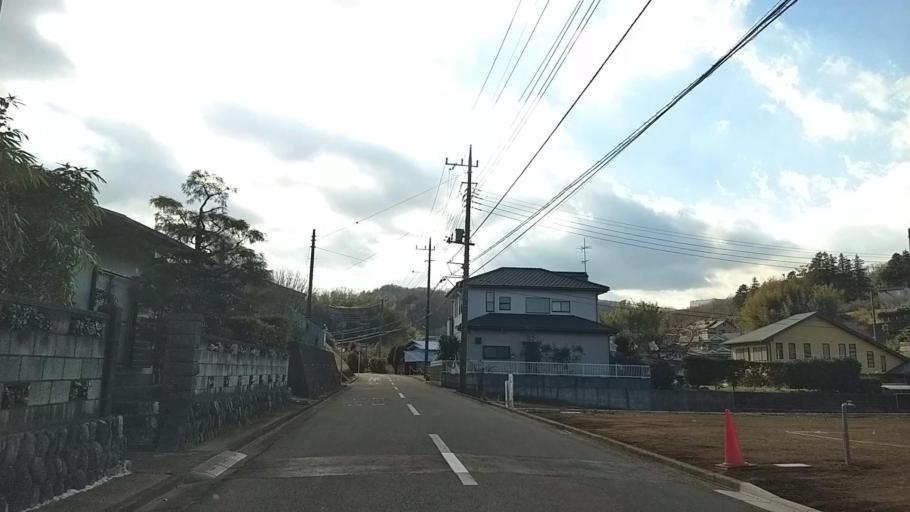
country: JP
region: Kanagawa
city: Isehara
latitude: 35.4305
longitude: 139.3180
